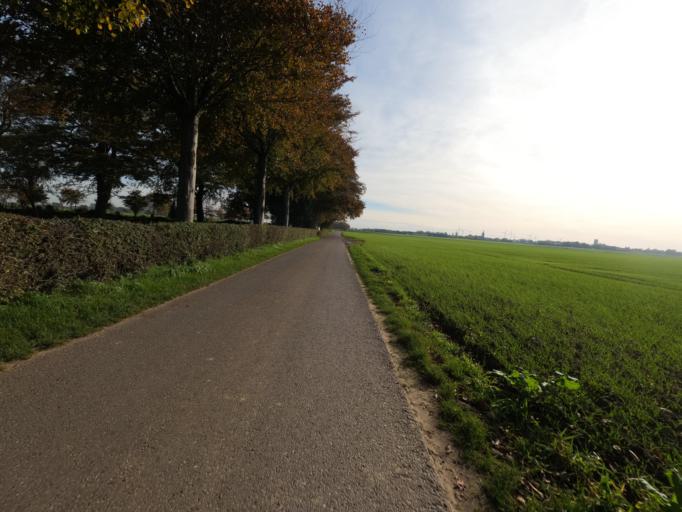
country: DE
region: North Rhine-Westphalia
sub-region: Regierungsbezirk Koln
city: Titz
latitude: 51.0600
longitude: 6.3926
